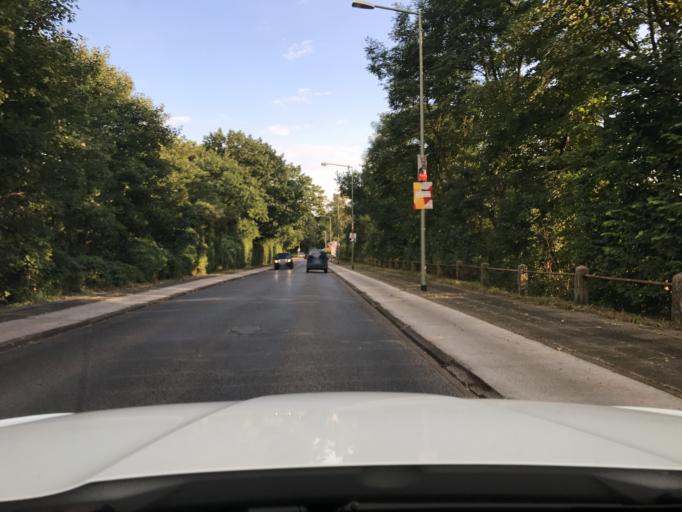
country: DE
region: North Rhine-Westphalia
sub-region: Regierungsbezirk Dusseldorf
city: Duisburg
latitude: 51.3991
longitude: 6.8045
